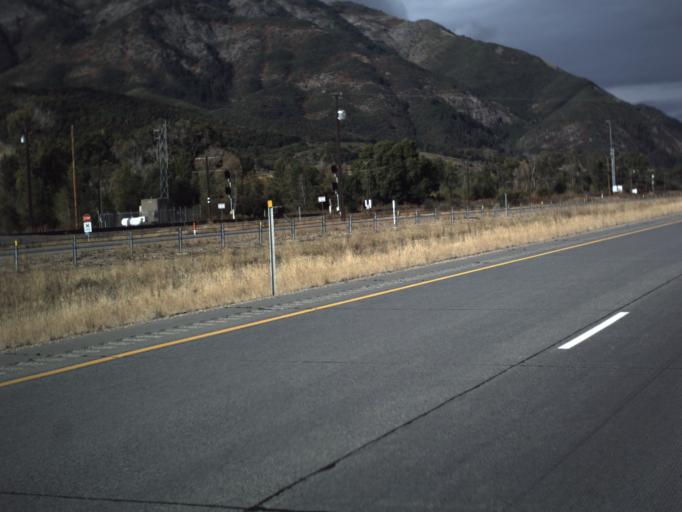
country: US
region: Utah
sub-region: Morgan County
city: Mountain Green
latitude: 41.1372
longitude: -111.7926
